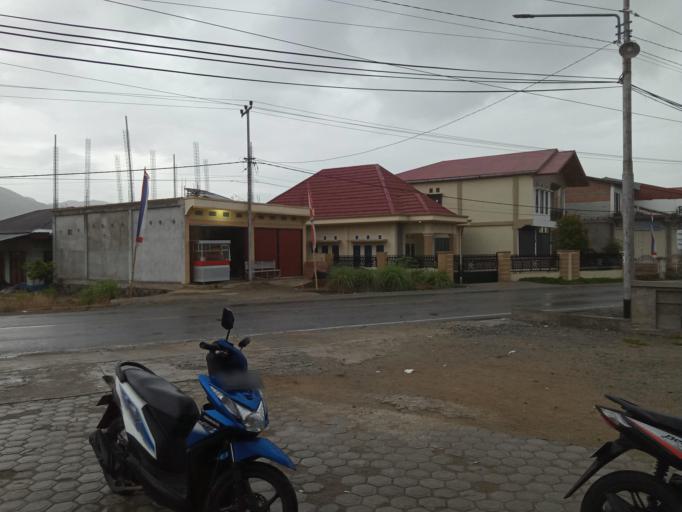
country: ID
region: Jambi
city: Semurup
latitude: -1.9995
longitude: 101.3771
